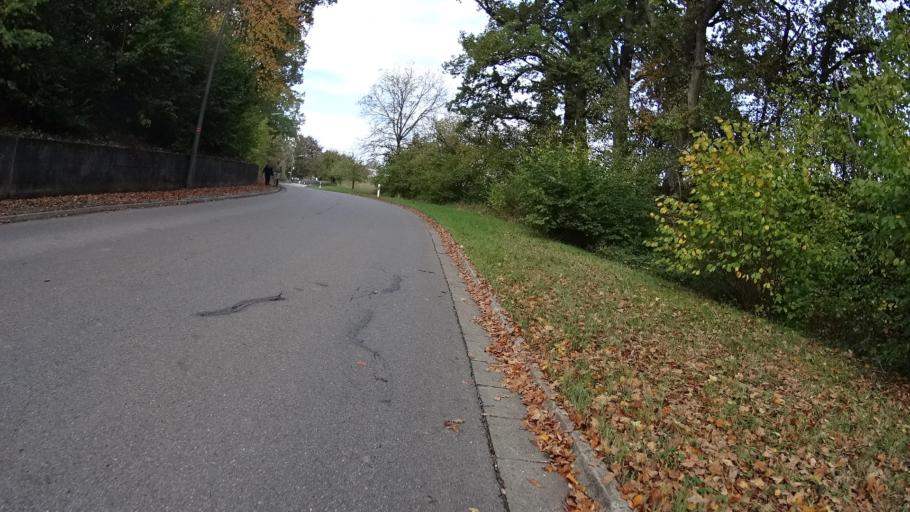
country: DE
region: Bavaria
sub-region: Upper Bavaria
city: Buxheim
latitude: 48.8271
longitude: 11.2754
